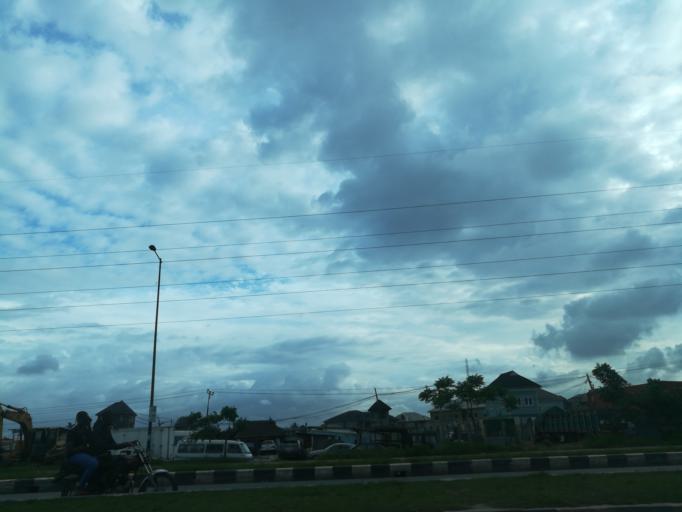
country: NG
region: Lagos
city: Ojota
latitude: 6.6115
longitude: 3.4188
